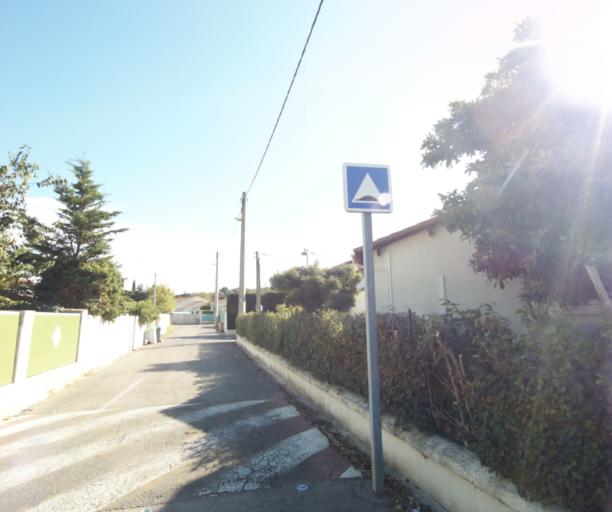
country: FR
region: Provence-Alpes-Cote d'Azur
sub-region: Departement des Bouches-du-Rhone
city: Saint-Victoret
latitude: 43.4160
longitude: 5.2468
